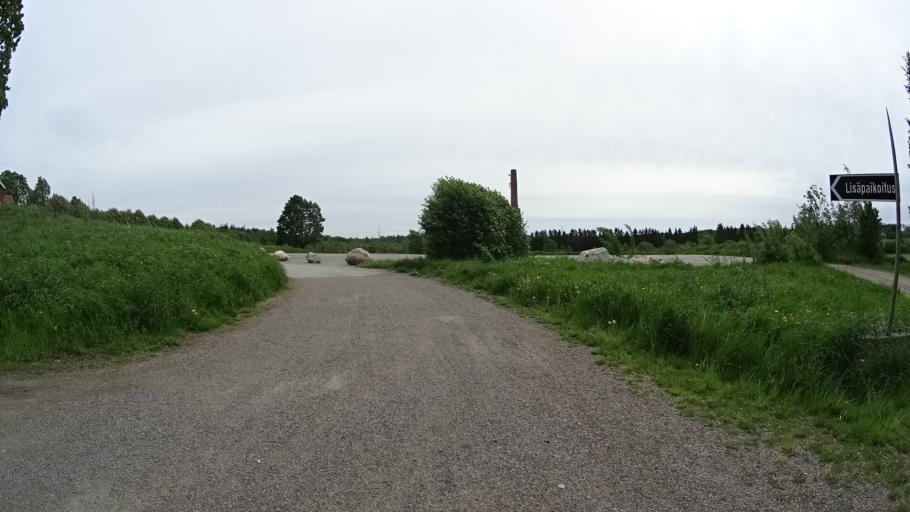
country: FI
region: Uusimaa
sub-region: Helsinki
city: Vantaa
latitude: 60.2842
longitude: 24.9498
